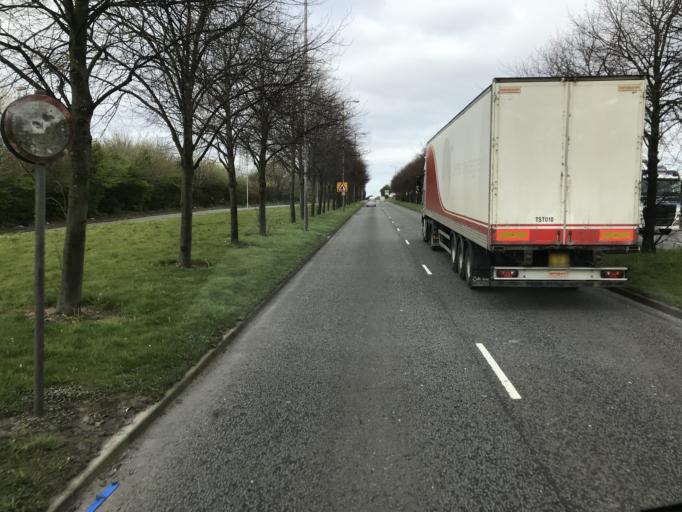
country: GB
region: England
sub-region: Borough of Halton
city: Hale
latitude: 53.3472
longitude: -2.8405
